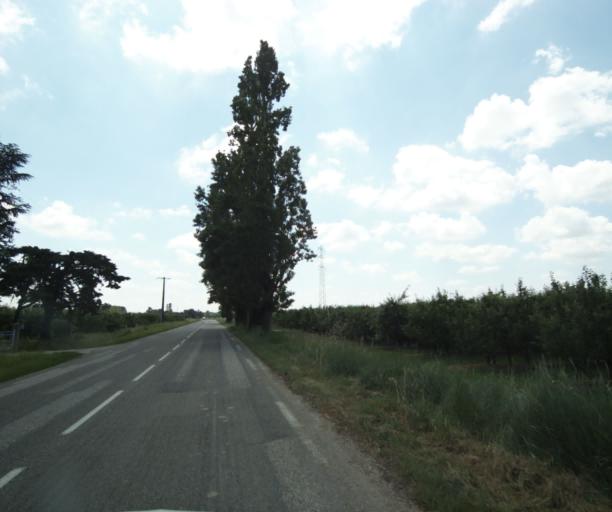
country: FR
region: Midi-Pyrenees
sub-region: Departement du Tarn-et-Garonne
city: Montauban
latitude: 44.0664
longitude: 1.3559
